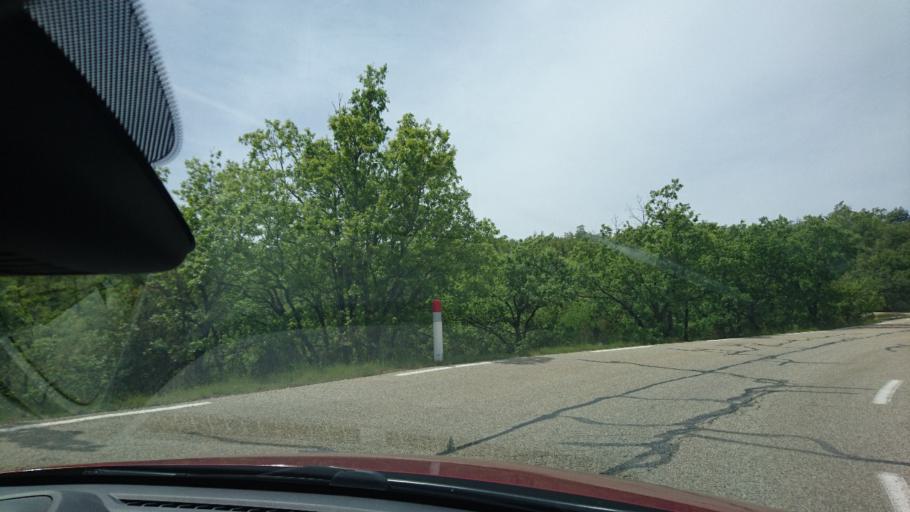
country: FR
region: Provence-Alpes-Cote d'Azur
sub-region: Departement du Vaucluse
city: Sault
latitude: 44.1118
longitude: 5.3935
